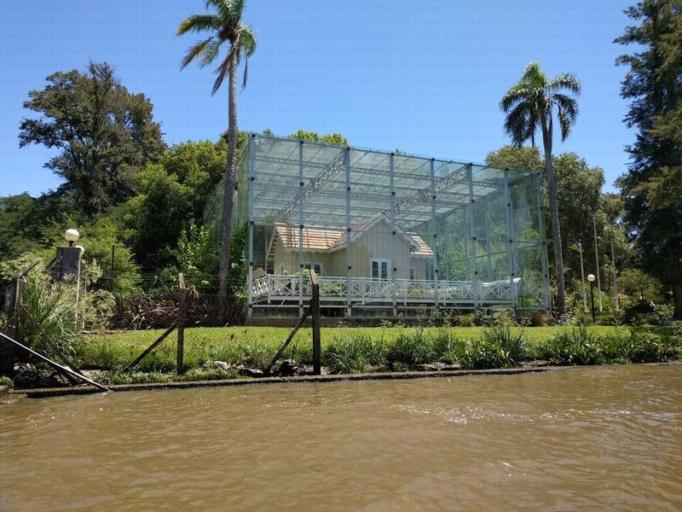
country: AR
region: Buenos Aires
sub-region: Partido de Tigre
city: Tigre
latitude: -34.3832
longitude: -58.5765
